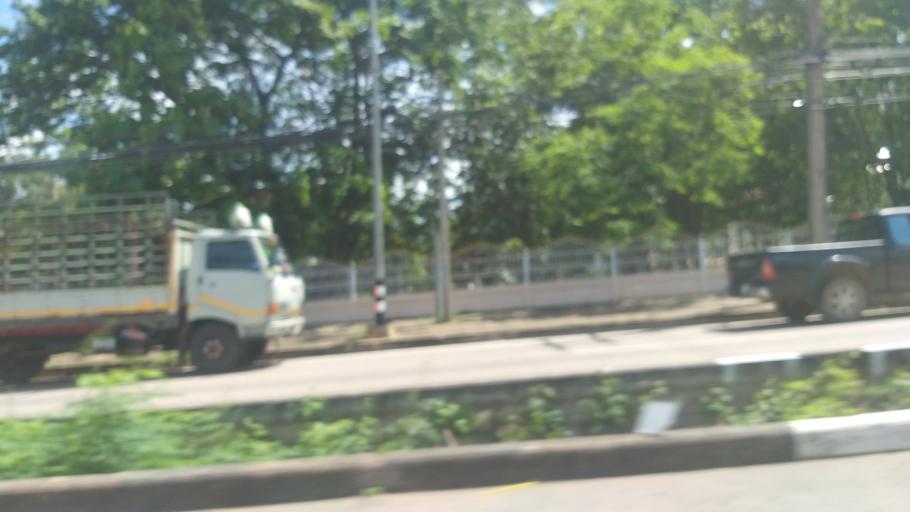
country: TH
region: Khon Kaen
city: Nong Ruea
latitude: 16.4908
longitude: 102.4418
